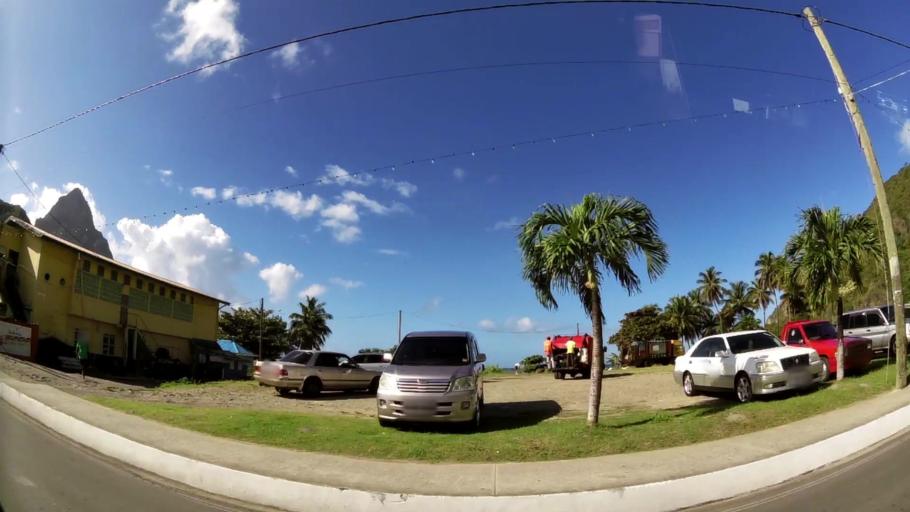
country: LC
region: Soufriere
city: Soufriere
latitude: 13.8556
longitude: -61.0596
